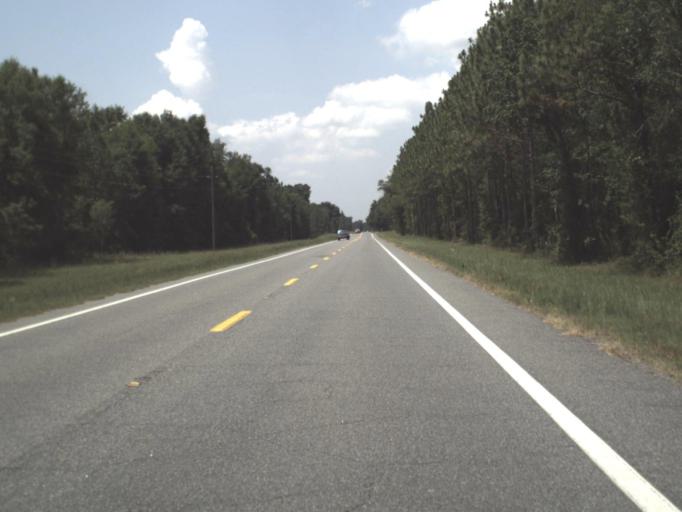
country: US
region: Florida
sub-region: Hamilton County
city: Jasper
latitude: 30.5043
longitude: -83.0696
